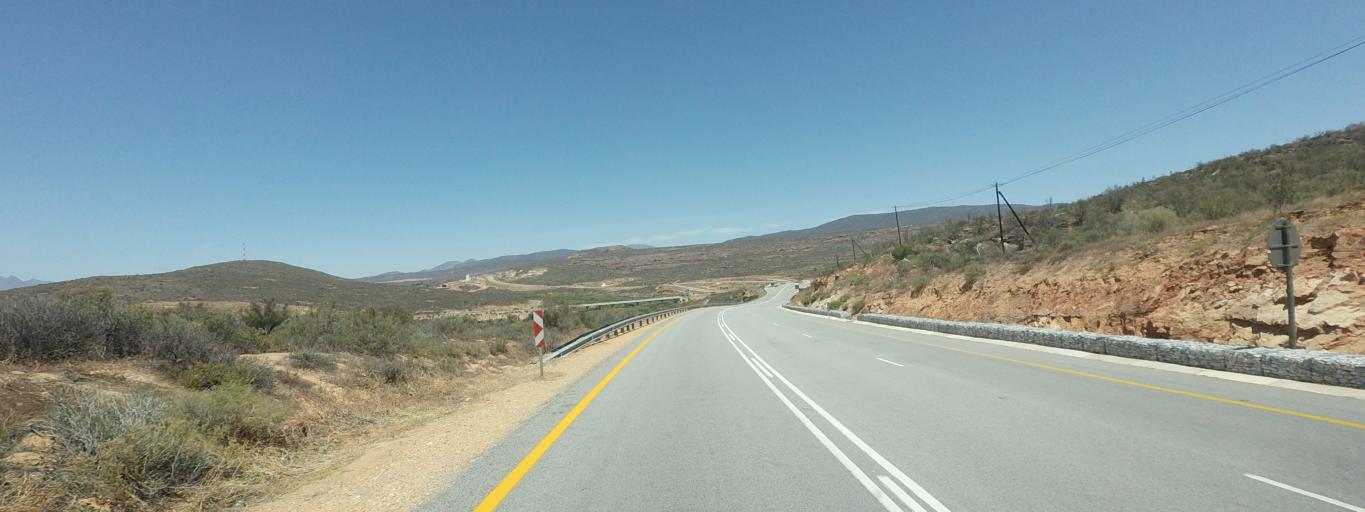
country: ZA
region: Western Cape
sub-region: West Coast District Municipality
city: Clanwilliam
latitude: -32.1663
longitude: 18.8716
